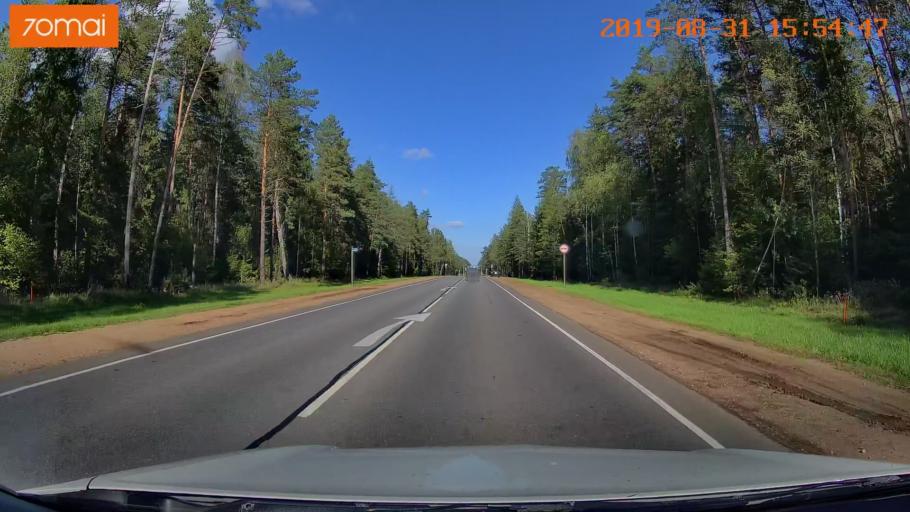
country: RU
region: Kaluga
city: Yukhnov
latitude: 54.7212
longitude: 35.1579
